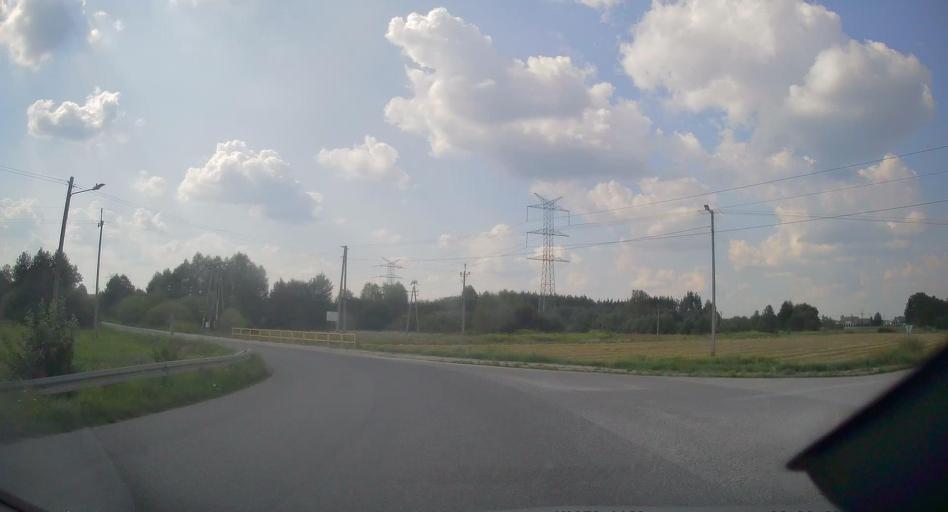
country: PL
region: Swietokrzyskie
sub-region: Powiat jedrzejowski
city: Malogoszcz
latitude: 50.8667
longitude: 20.3220
